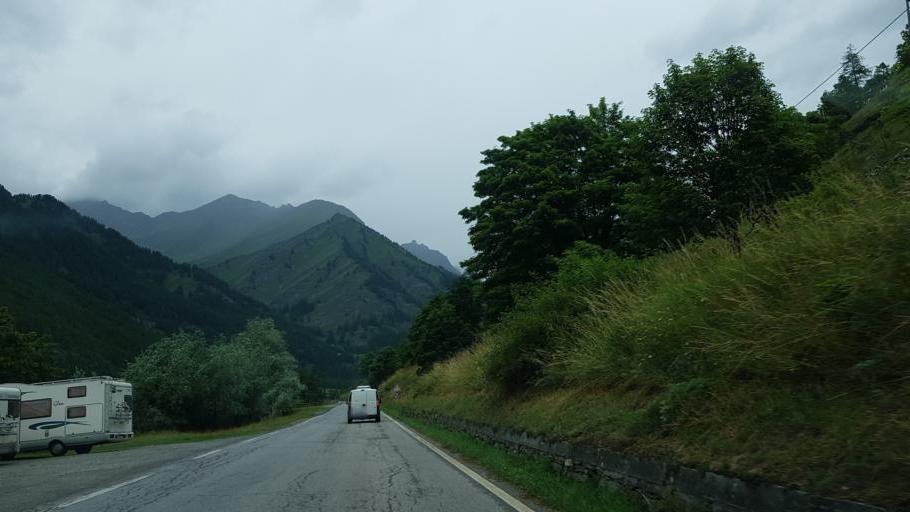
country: IT
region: Piedmont
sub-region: Provincia di Cuneo
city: Pontechianale
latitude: 44.6168
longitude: 7.0430
